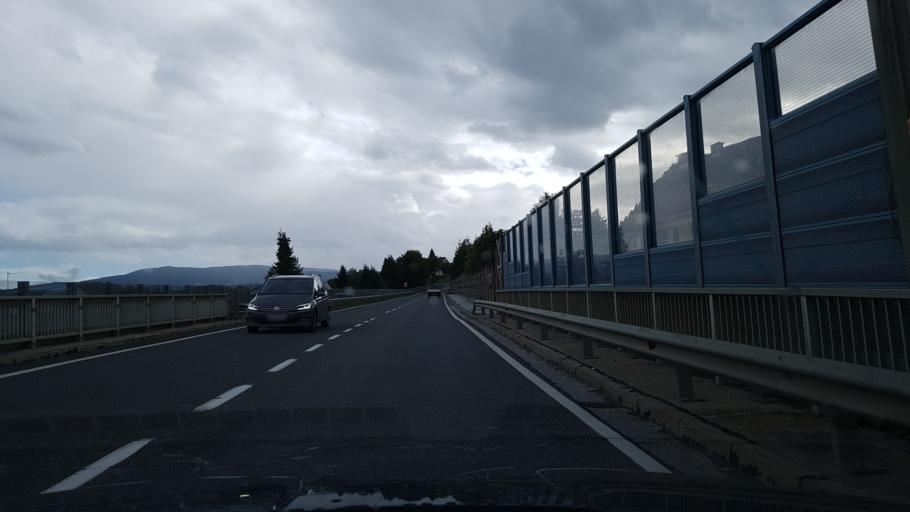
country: AT
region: Styria
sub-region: Politischer Bezirk Voitsberg
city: Koflach
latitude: 47.0652
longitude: 15.0735
